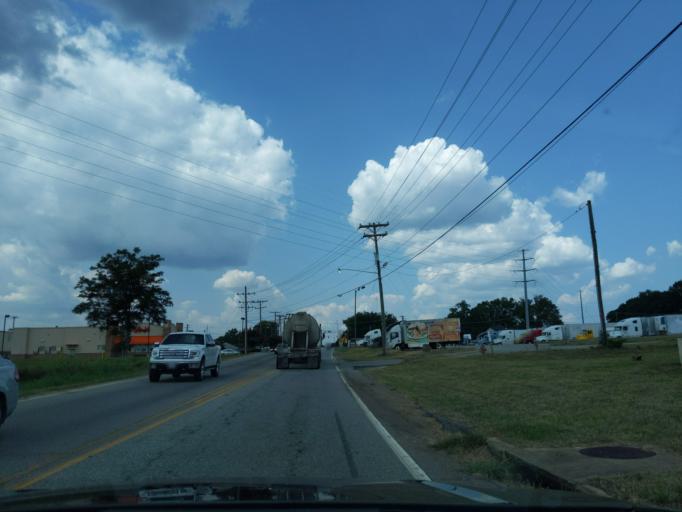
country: US
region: South Carolina
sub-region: Greenville County
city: Fountain Inn
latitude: 34.6867
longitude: -82.1966
